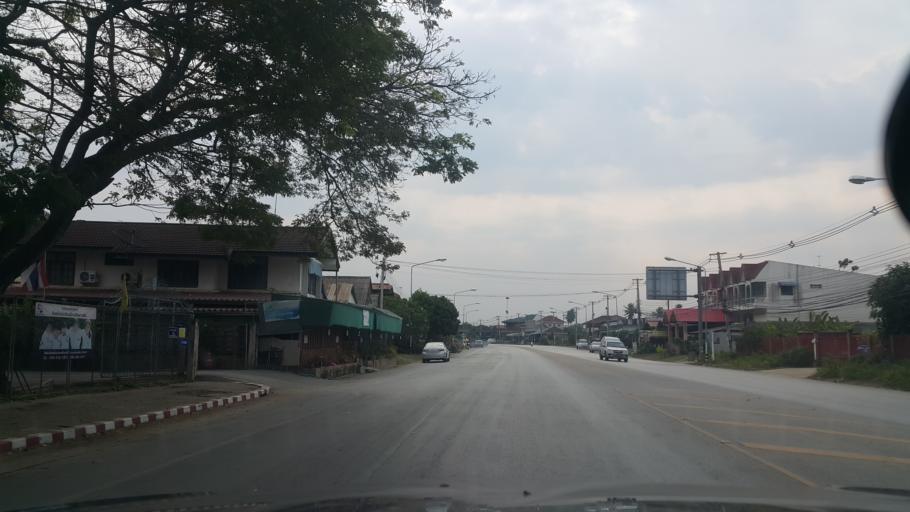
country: TH
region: Sukhothai
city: Si Samrong
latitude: 17.1624
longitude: 99.8627
